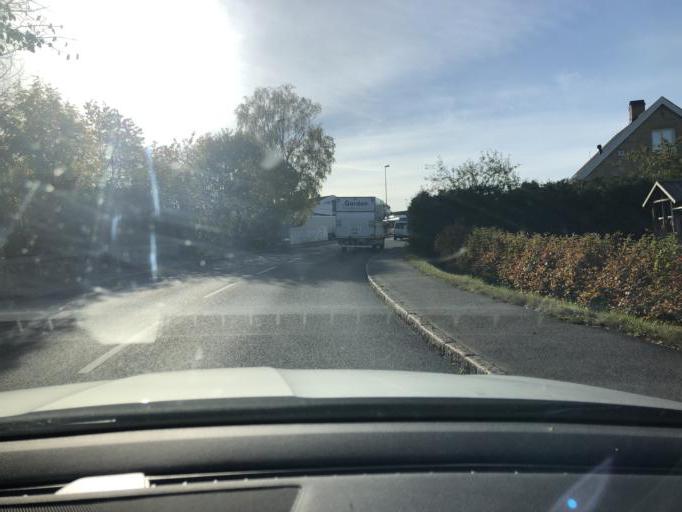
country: SE
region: Joenkoeping
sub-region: Jonkopings Kommun
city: Jonkoping
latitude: 57.7744
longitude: 14.1263
